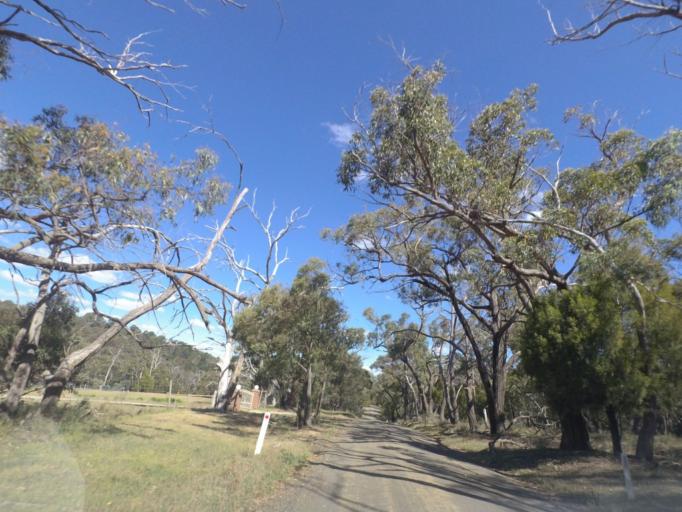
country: AU
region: Victoria
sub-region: Hume
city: Sunbury
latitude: -37.4350
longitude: 144.6616
